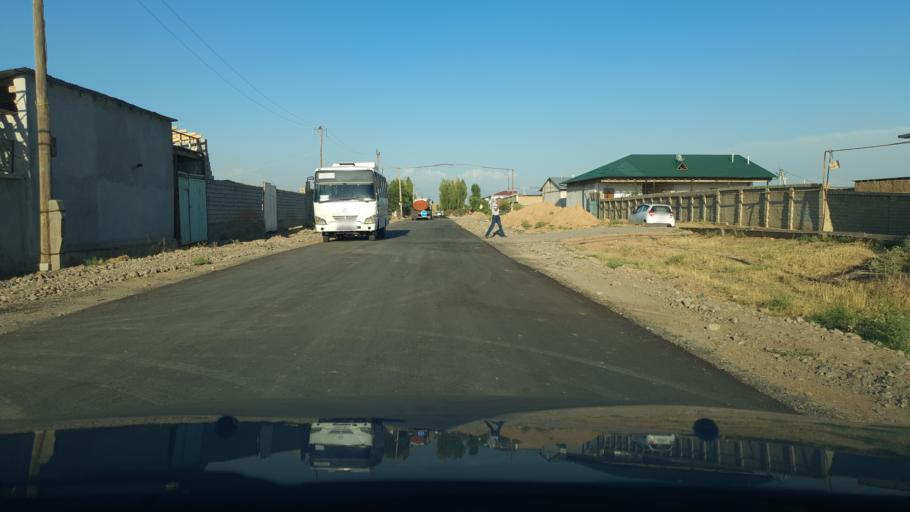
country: UZ
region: Toshkent
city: Salor
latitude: 41.4566
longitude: 69.4018
